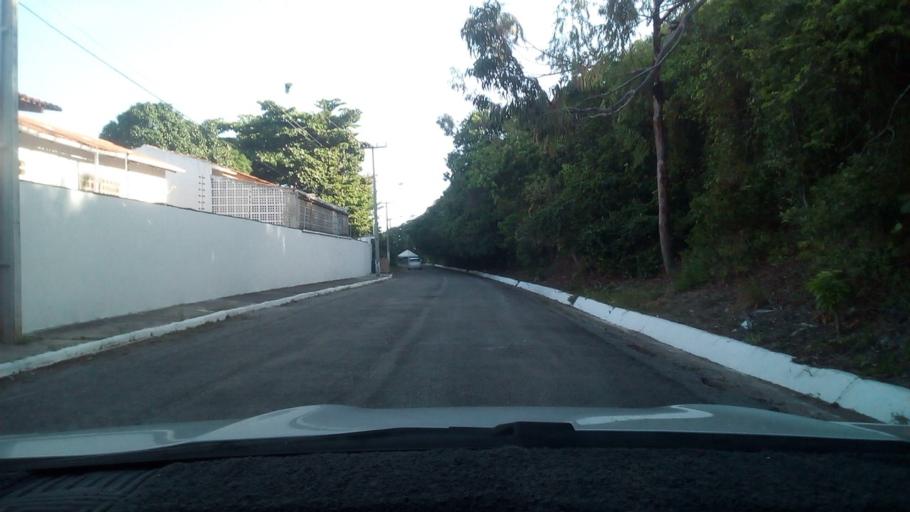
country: BR
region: Paraiba
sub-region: Joao Pessoa
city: Joao Pessoa
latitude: -7.1616
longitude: -34.7972
